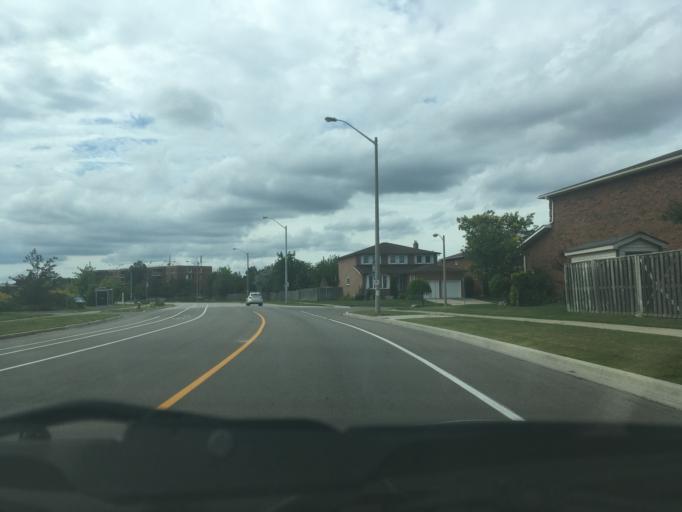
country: CA
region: Ontario
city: Brampton
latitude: 43.6635
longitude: -79.7208
